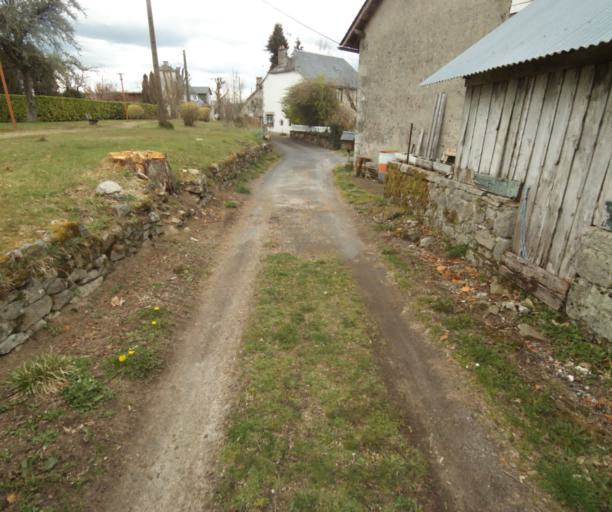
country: FR
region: Limousin
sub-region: Departement de la Correze
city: Correze
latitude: 45.3336
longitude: 1.9450
